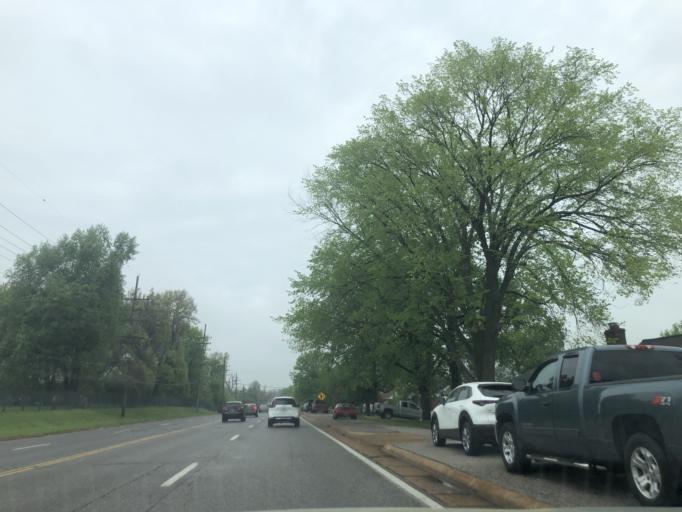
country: US
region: Missouri
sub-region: Saint Louis County
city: Marlborough
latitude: 38.5773
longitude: -90.3190
